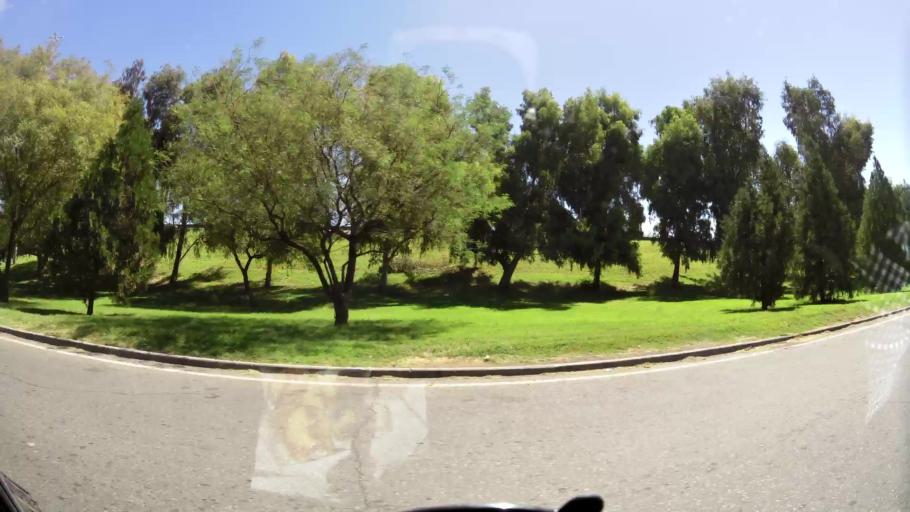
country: AR
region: San Juan
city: San Juan
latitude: -31.5207
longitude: -68.5361
